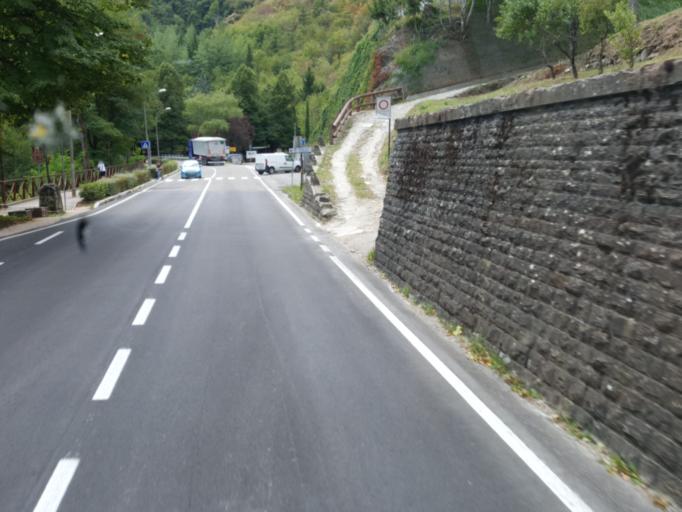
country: IT
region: Emilia-Romagna
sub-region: Forli-Cesena
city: San Piero in Bagno
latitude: 43.8322
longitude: 11.9565
